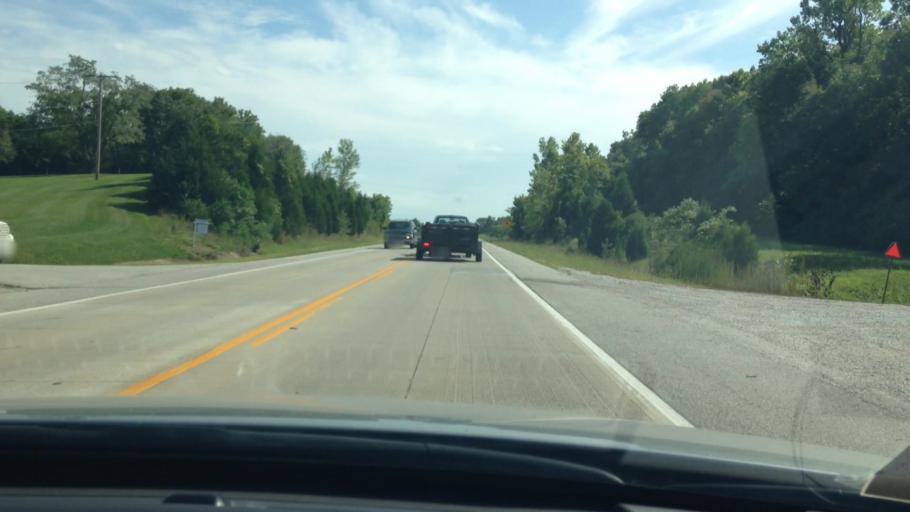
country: US
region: Missouri
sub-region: Jackson County
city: Grandview
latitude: 38.8585
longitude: -94.5858
